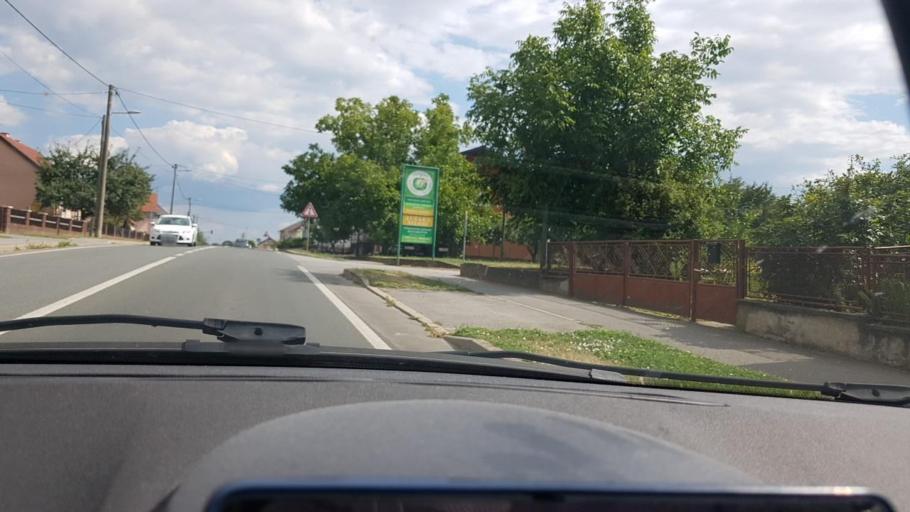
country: HR
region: Bjelovarsko-Bilogorska
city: Zdralovi
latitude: 45.8852
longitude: 16.8645
